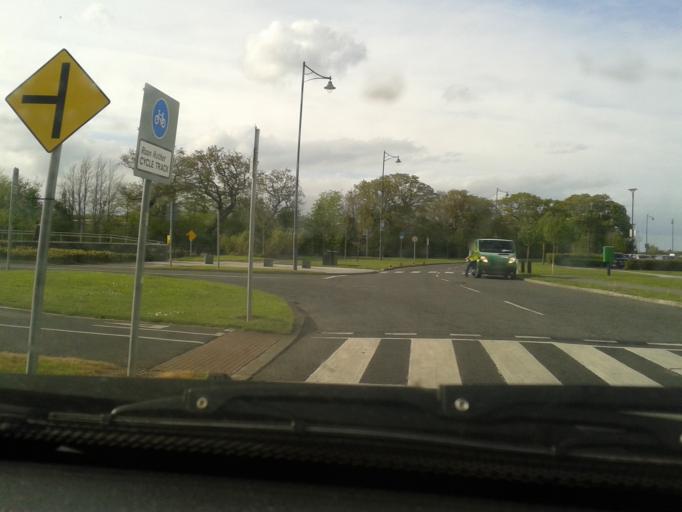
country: IE
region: Leinster
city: Ballymun
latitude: 53.4033
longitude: -6.2584
